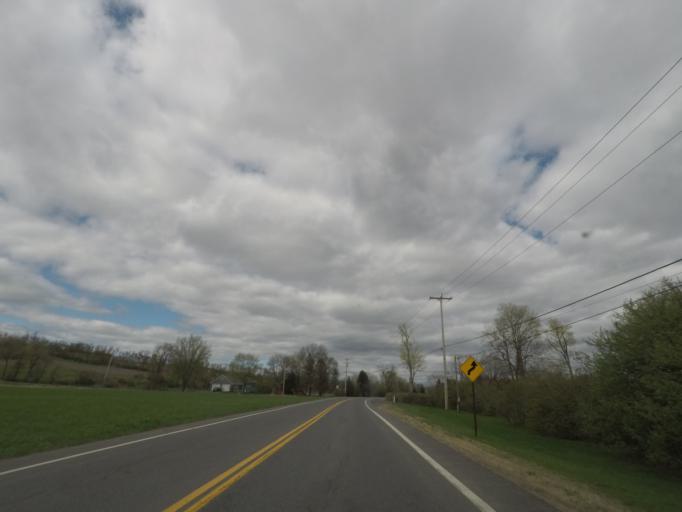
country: US
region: New York
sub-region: Columbia County
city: Philmont
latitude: 42.2912
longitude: -73.6465
